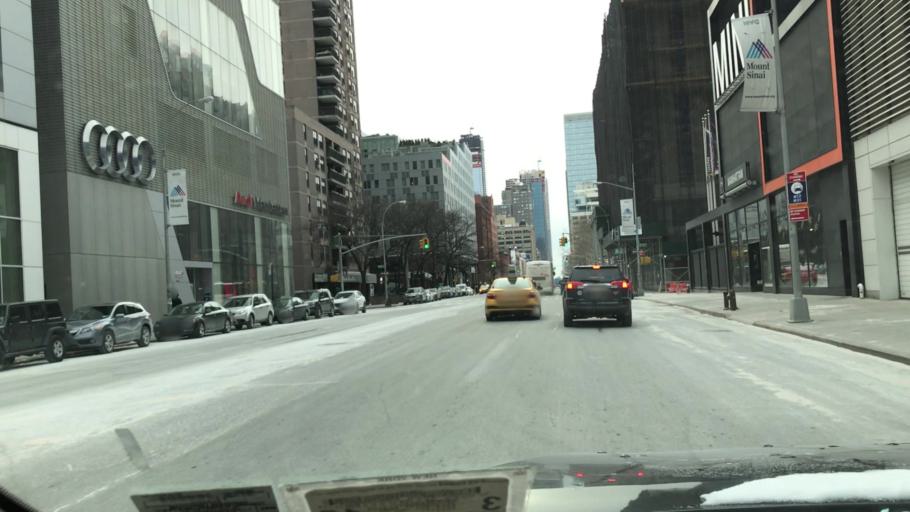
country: US
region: New Jersey
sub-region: Hudson County
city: Guttenberg
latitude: 40.7696
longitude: -73.9920
